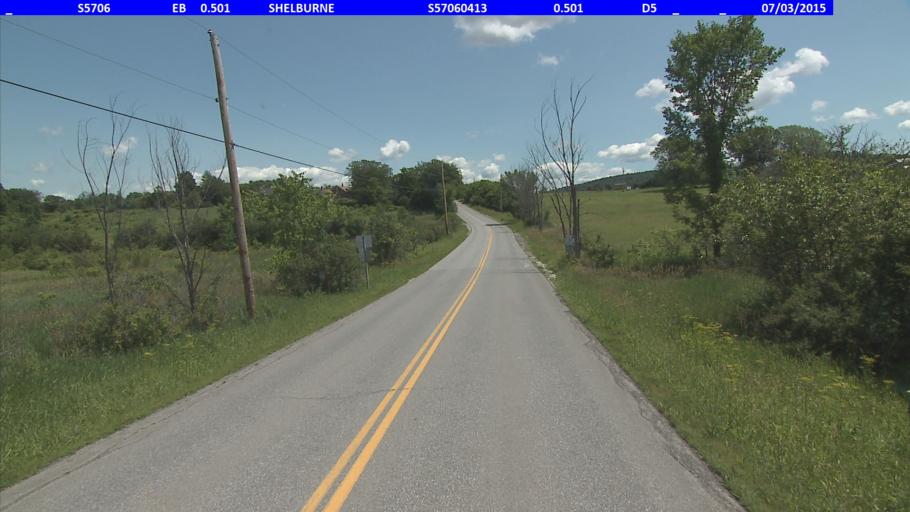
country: US
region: Vermont
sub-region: Chittenden County
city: South Burlington
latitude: 44.4085
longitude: -73.1679
